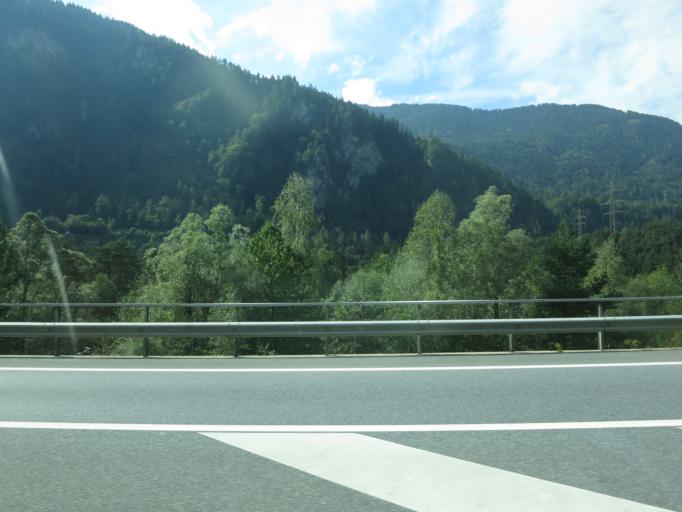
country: CH
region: Grisons
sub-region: Imboden District
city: Rhazuns
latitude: 46.7796
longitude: 9.4162
